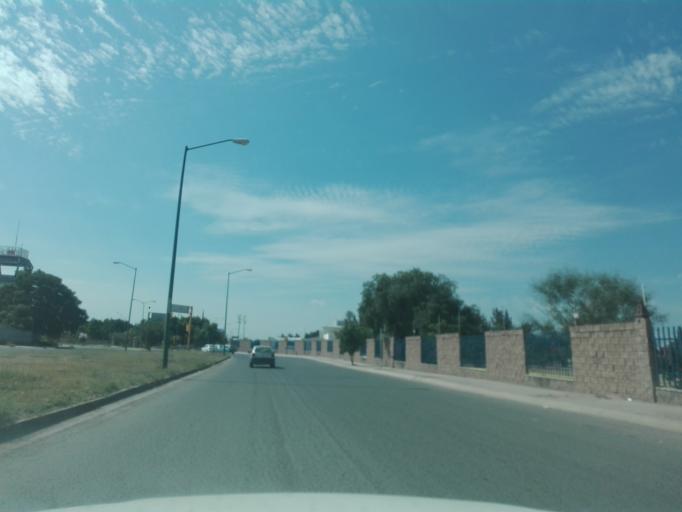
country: MX
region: Guanajuato
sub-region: Leon
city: Ladrilleras del Refugio
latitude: 21.0618
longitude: -101.5787
